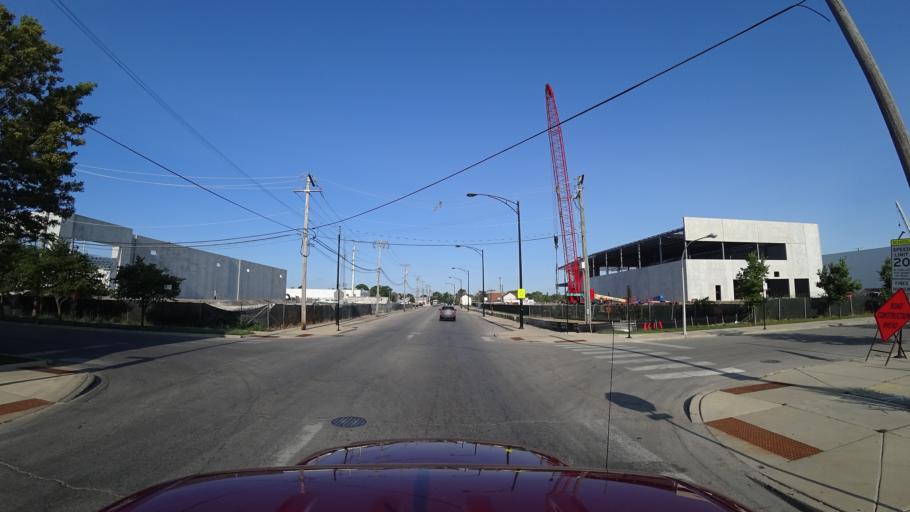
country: US
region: Illinois
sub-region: Cook County
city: Cicero
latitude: 41.8007
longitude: -87.7109
